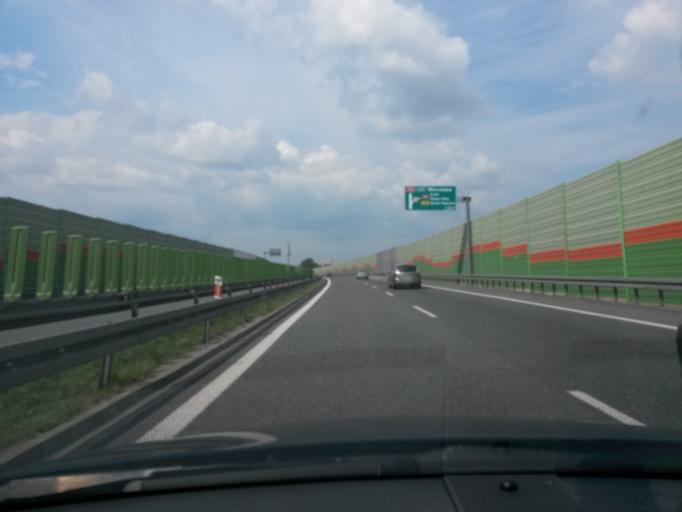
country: PL
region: Lodz Voivodeship
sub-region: Powiat rawski
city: Rawa Mazowiecka
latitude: 51.7653
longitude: 20.2697
